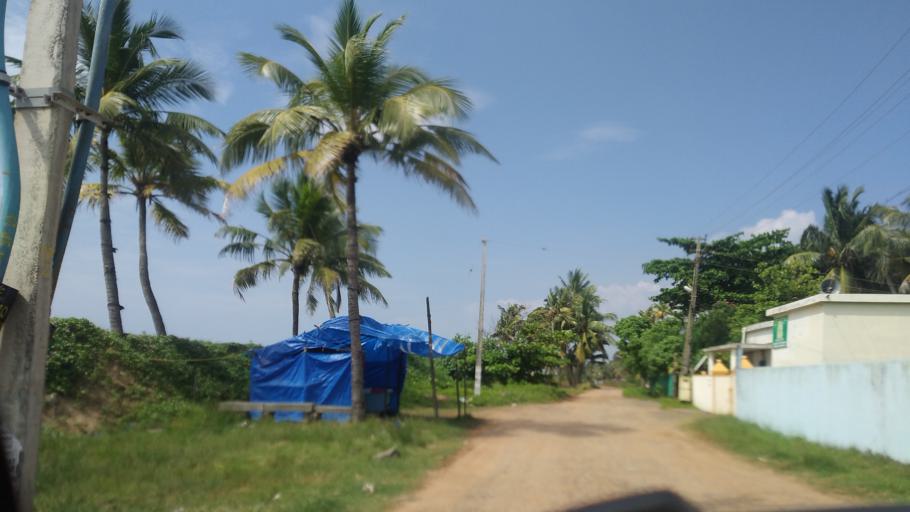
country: IN
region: Kerala
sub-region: Ernakulam
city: Elur
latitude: 10.0606
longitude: 76.2000
